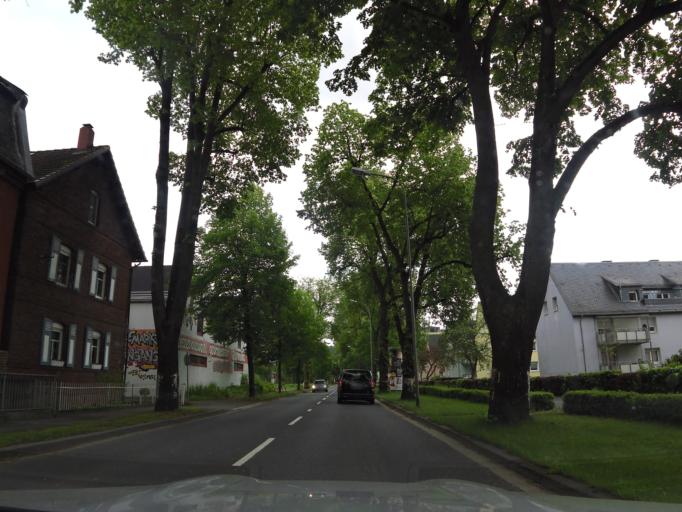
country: DE
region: Hesse
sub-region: Regierungsbezirk Giessen
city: Wetzlar
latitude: 50.5502
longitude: 8.4823
